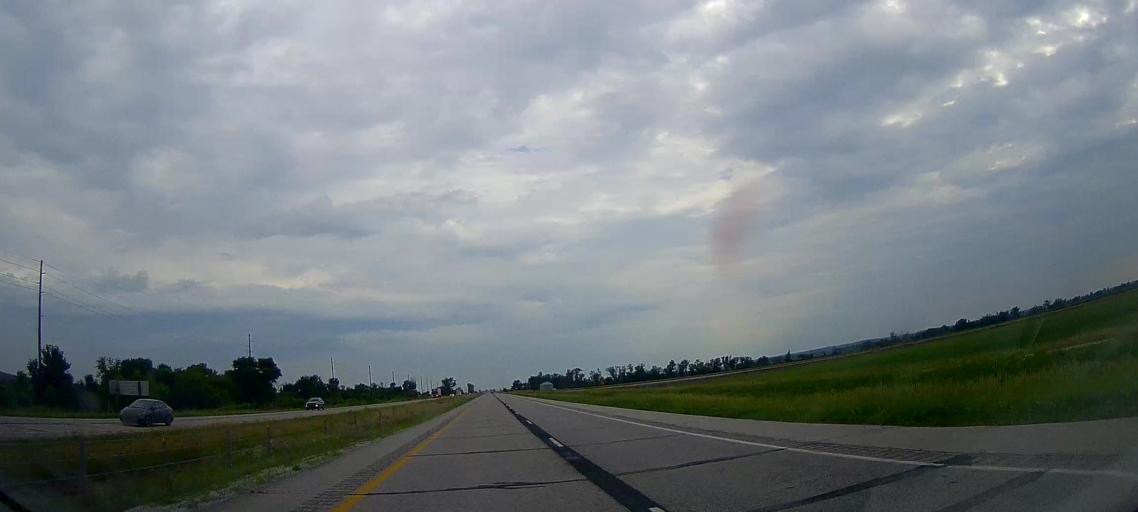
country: US
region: Iowa
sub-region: Harrison County
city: Missouri Valley
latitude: 41.4737
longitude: -95.8997
